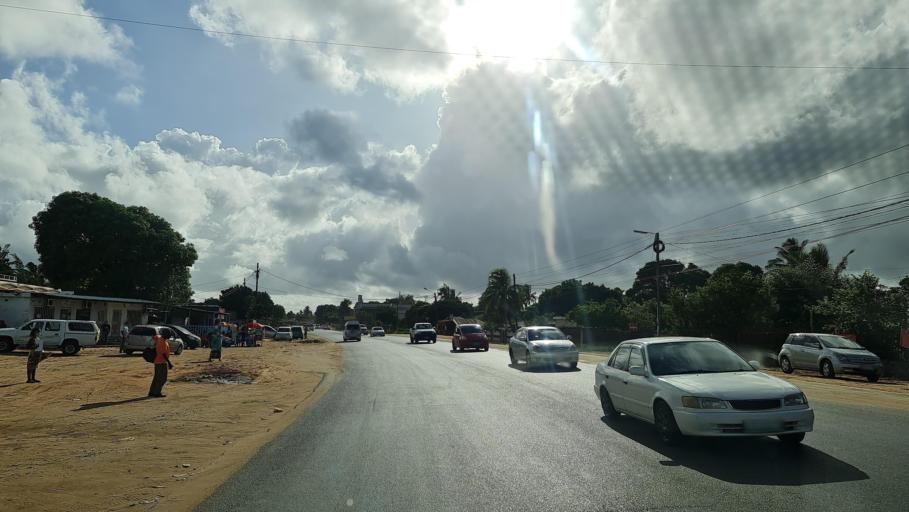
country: MZ
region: Gaza
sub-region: Xai-Xai District
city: Xai-Xai
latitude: -25.0569
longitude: 33.6636
